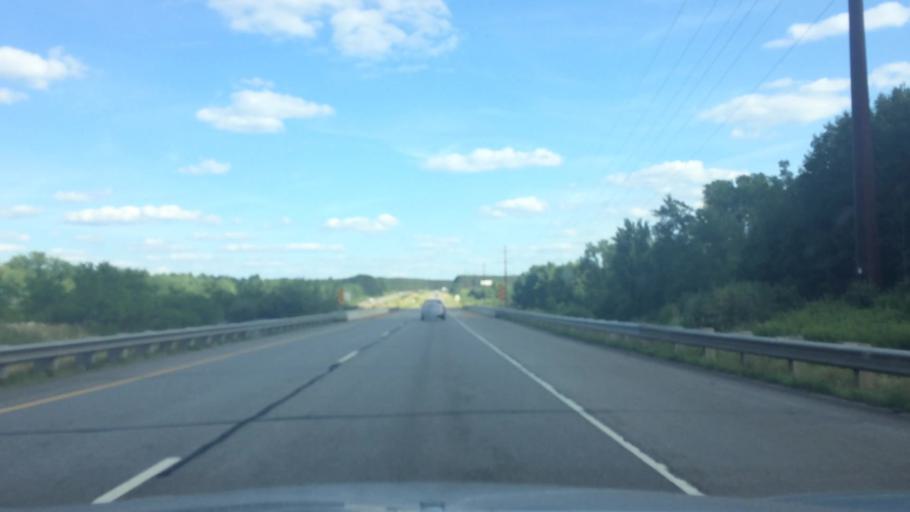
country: US
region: Wisconsin
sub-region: Lincoln County
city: Merrill
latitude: 45.2058
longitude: -89.6614
